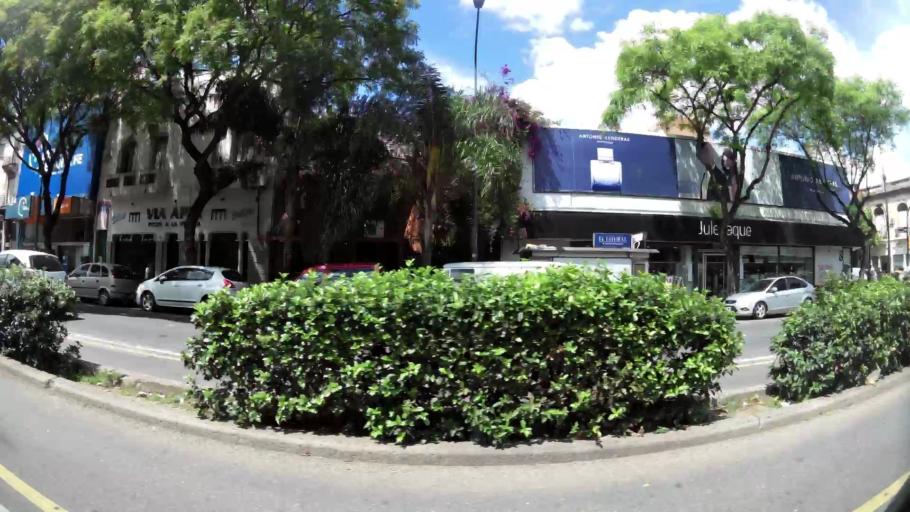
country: AR
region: Santa Fe
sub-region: Departamento de Rosario
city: Rosario
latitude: -32.9576
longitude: -60.6391
